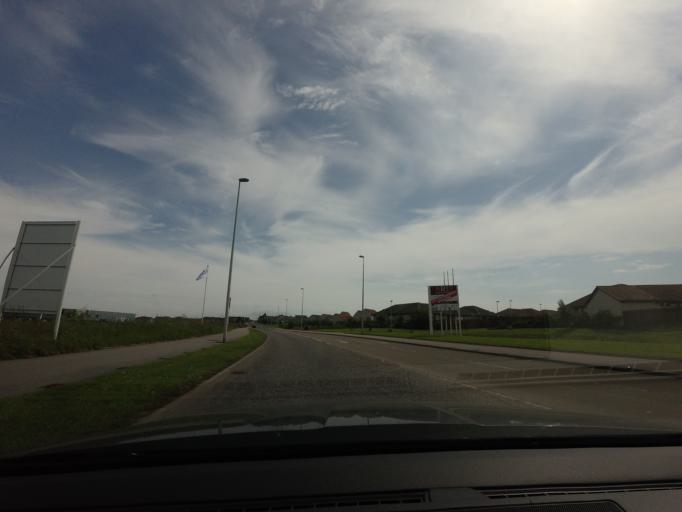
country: GB
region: Scotland
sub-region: Aberdeenshire
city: Peterhead
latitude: 57.5070
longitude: -1.8220
